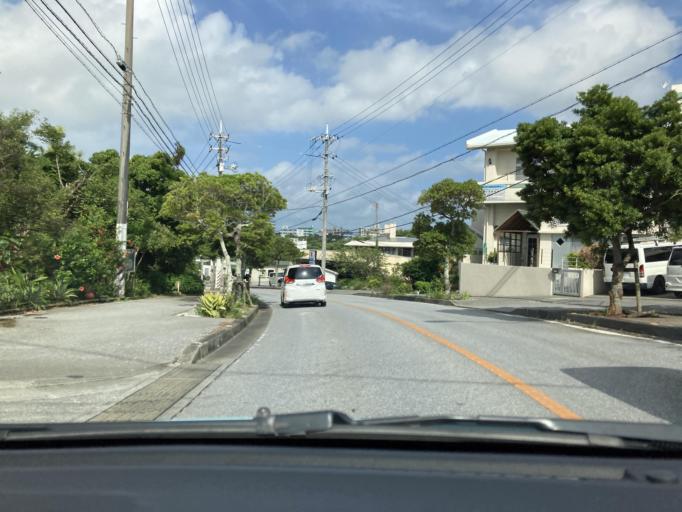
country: JP
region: Okinawa
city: Ginowan
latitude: 26.2617
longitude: 127.7767
